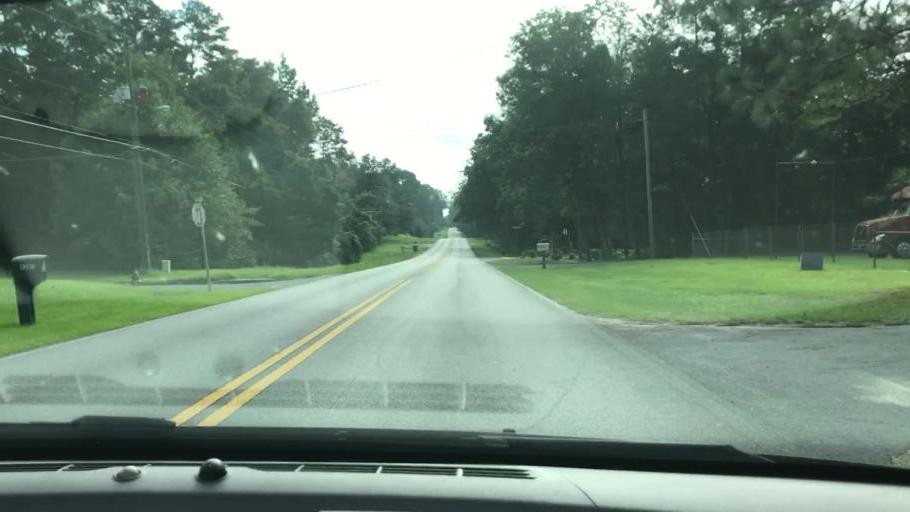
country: US
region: Florida
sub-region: Jackson County
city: Marianna
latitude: 30.7690
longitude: -85.2395
